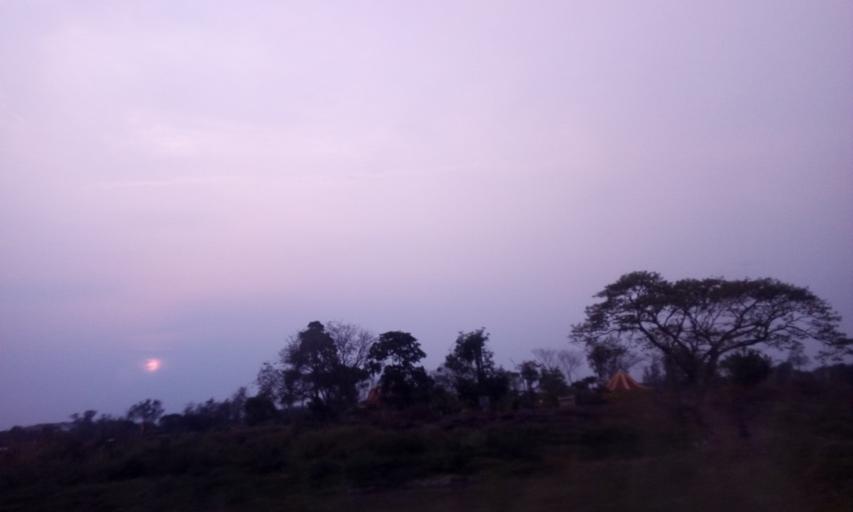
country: TH
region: Pathum Thani
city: Nong Suea
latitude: 14.0708
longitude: 100.8950
